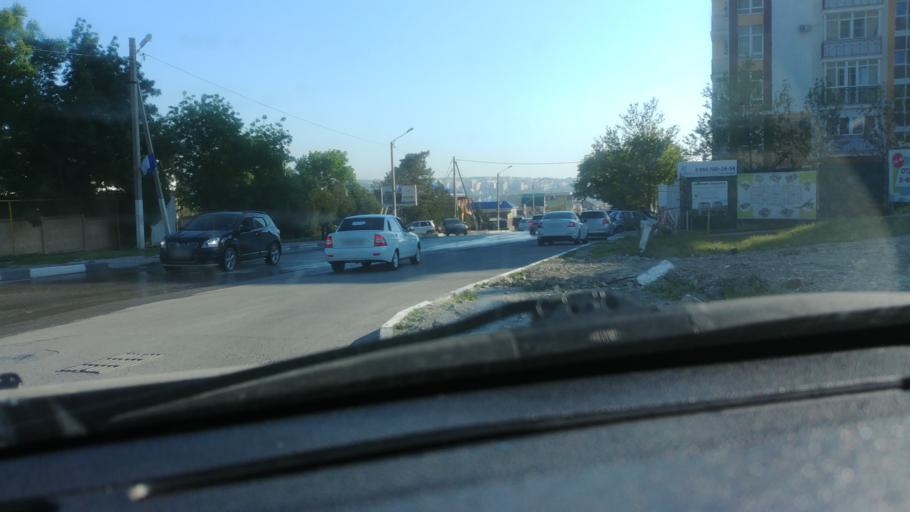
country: RU
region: Krasnodarskiy
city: Gelendzhik
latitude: 44.5715
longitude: 38.0929
